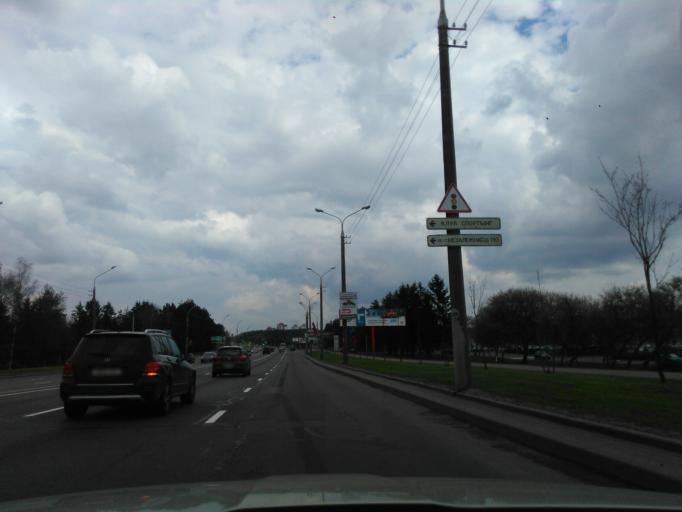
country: BY
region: Minsk
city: Lyeskawka
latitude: 53.9527
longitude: 27.7116
